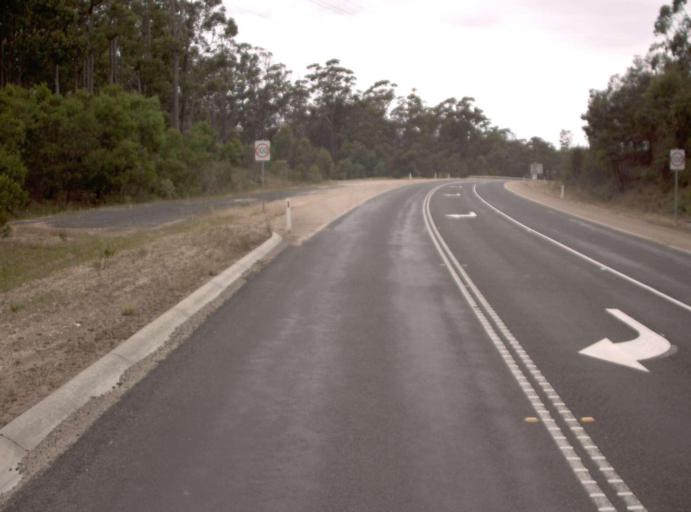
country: AU
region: Victoria
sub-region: East Gippsland
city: Lakes Entrance
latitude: -37.6920
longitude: 148.0417
